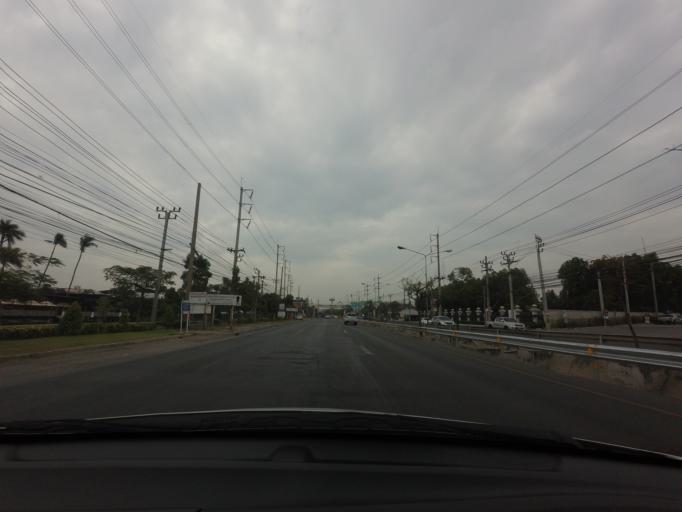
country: TH
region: Samut Prakan
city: Samut Prakan
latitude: 13.5413
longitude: 100.6204
